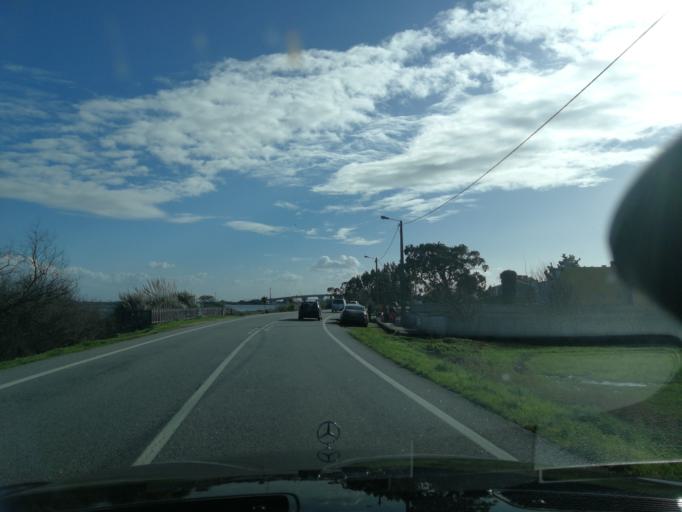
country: PT
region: Aveiro
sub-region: Estarreja
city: Pardilho
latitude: 40.7963
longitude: -8.6735
